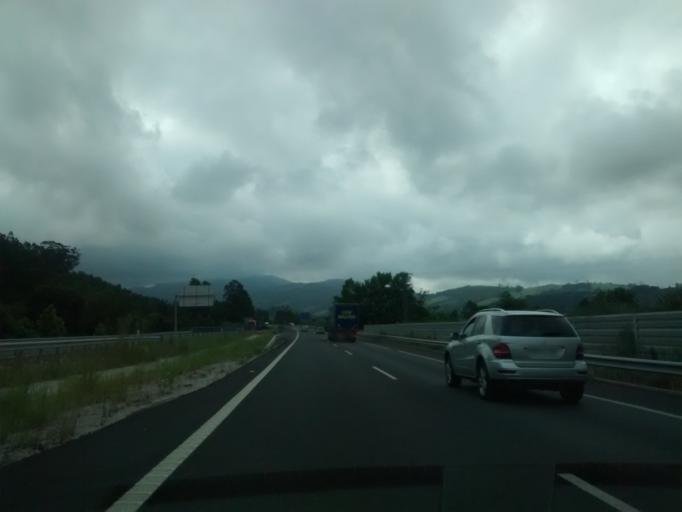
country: ES
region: Cantabria
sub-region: Provincia de Cantabria
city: Puente Viesgo
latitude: 43.3251
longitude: -3.9585
